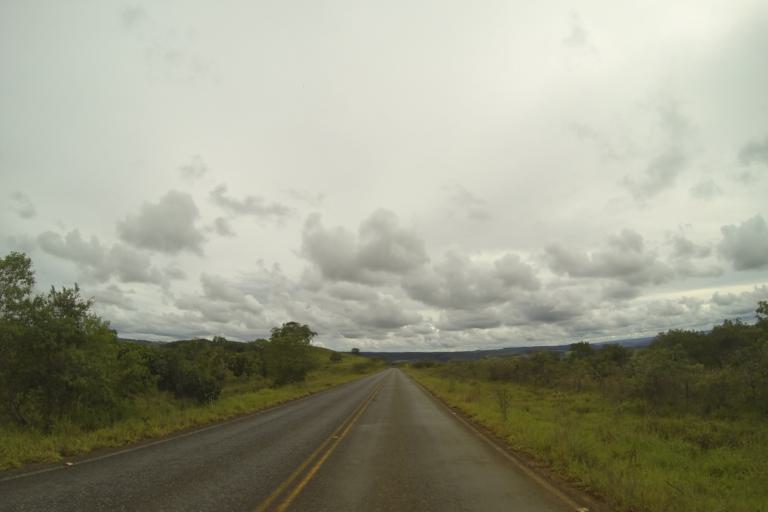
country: BR
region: Minas Gerais
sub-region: Ibia
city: Ibia
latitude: -19.6828
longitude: -46.4436
